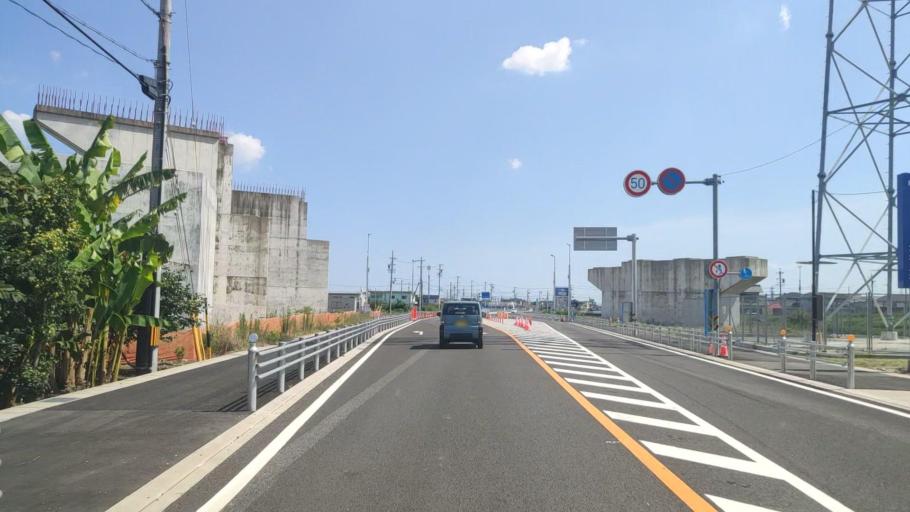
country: JP
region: Gifu
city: Godo
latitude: 35.4615
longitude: 136.6760
